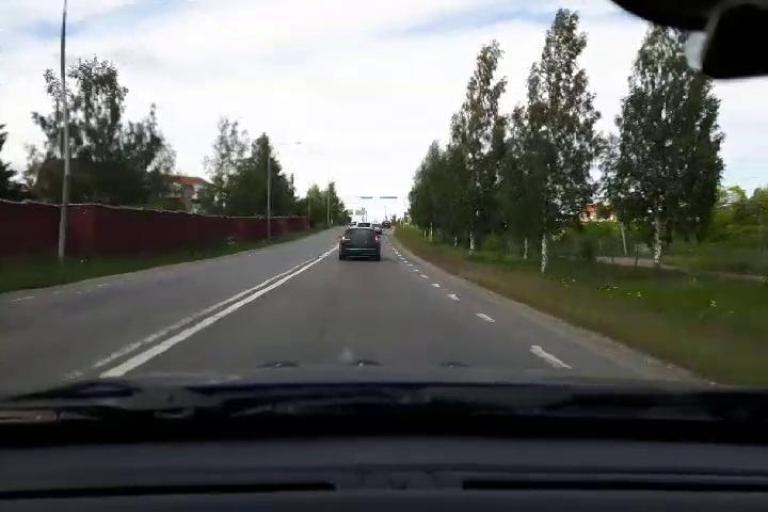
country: SE
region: Gaevleborg
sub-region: Bollnas Kommun
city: Bollnas
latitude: 61.3545
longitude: 16.3926
